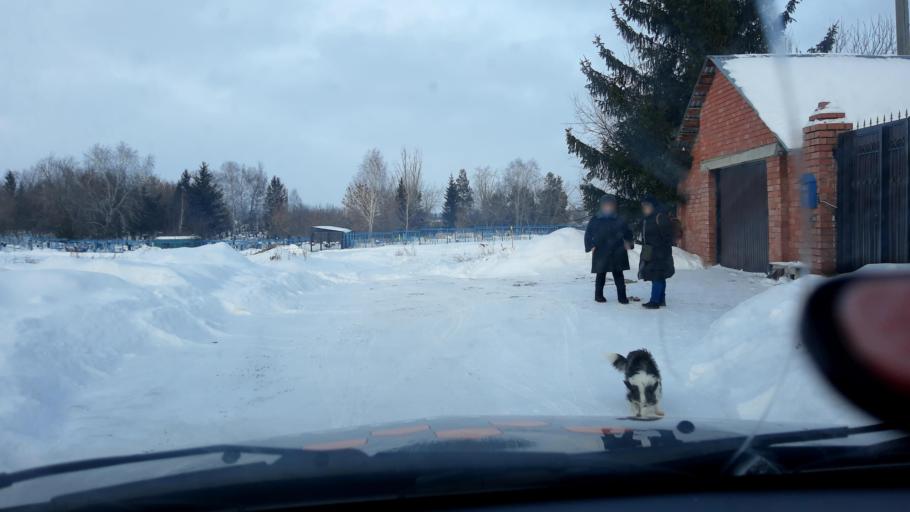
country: RU
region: Bashkortostan
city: Avdon
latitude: 54.4923
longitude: 55.8908
